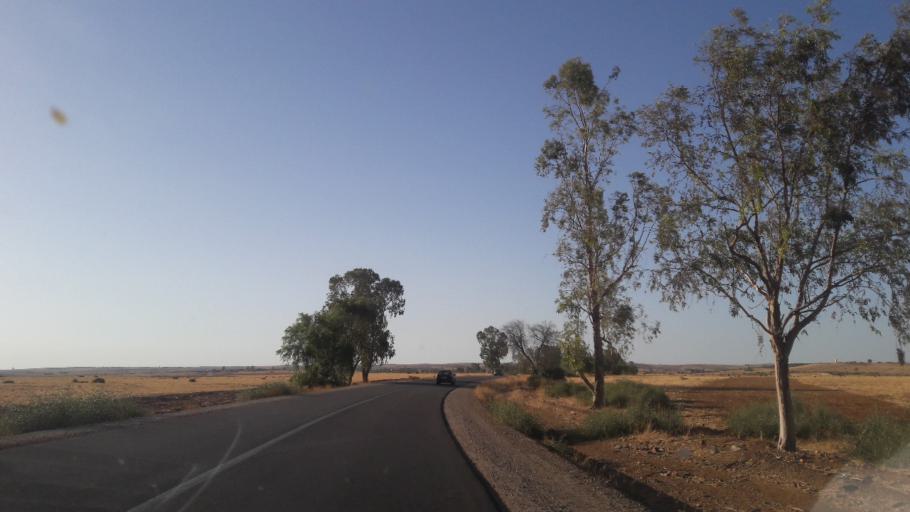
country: MA
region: Chaouia-Ouardigha
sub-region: Khouribga Province
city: Boujniba
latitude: 32.9889
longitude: -6.6831
